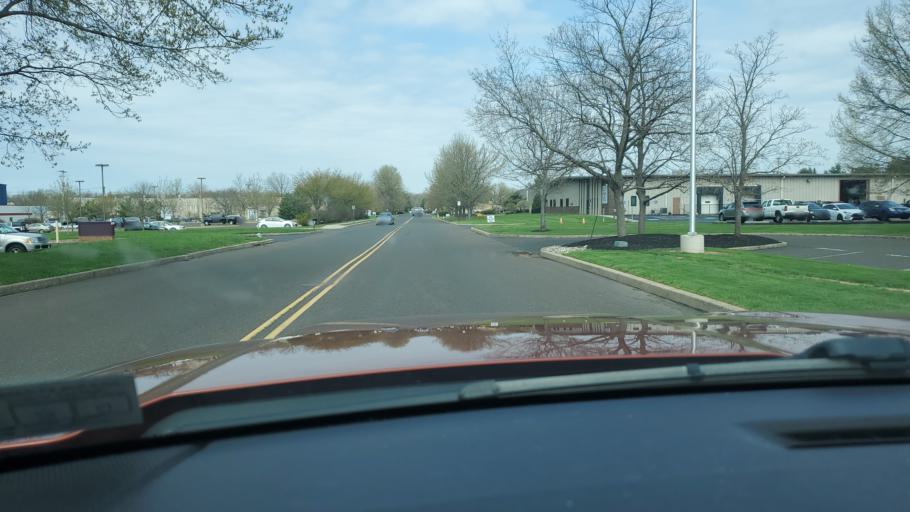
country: US
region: Pennsylvania
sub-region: Montgomery County
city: Hatfield
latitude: 40.2892
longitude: -75.2828
